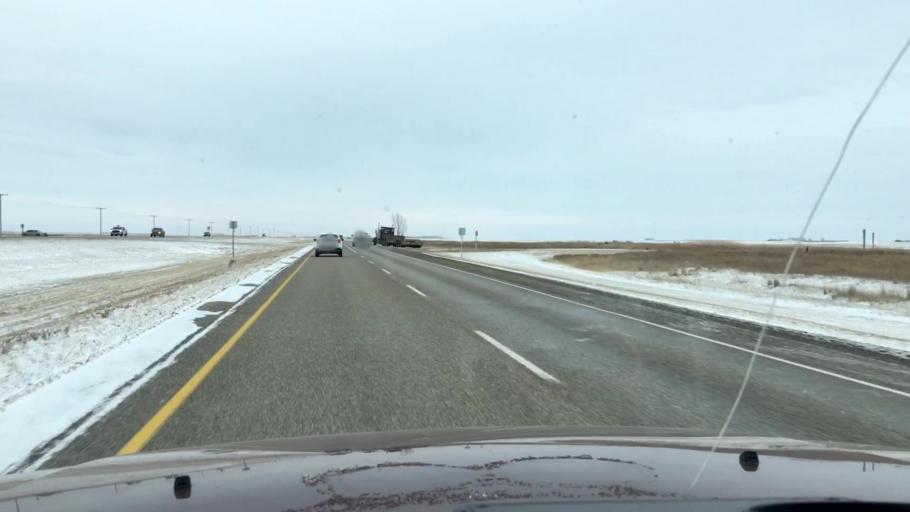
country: CA
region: Saskatchewan
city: Moose Jaw
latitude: 51.0092
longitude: -105.7739
